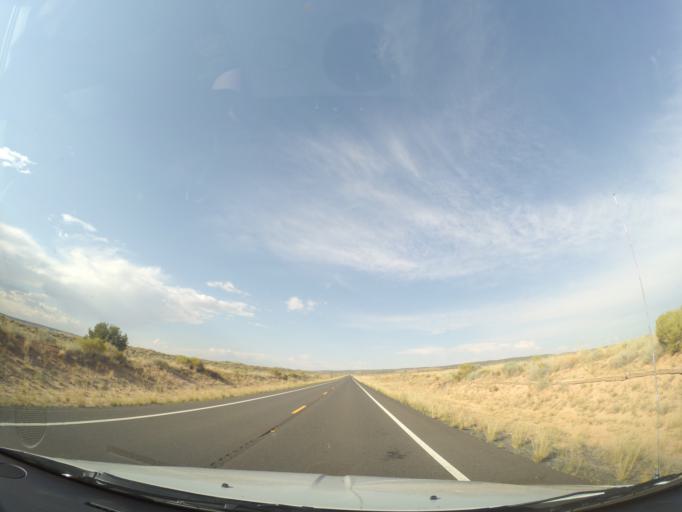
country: US
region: Arizona
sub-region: Coconino County
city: Kaibito
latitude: 36.4682
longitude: -111.4195
